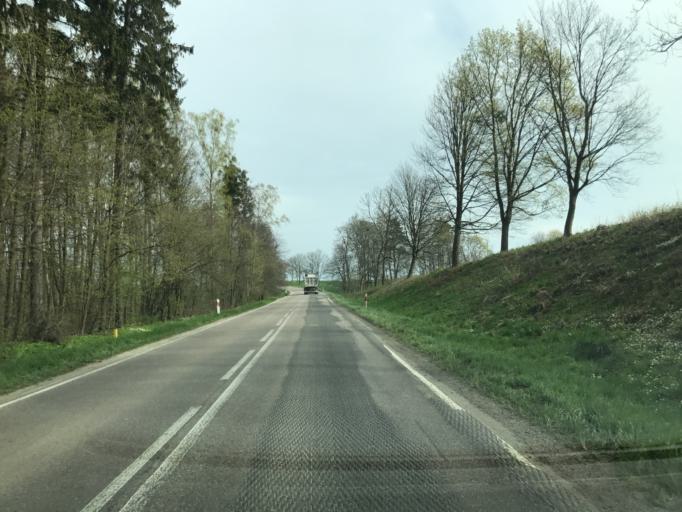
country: PL
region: Warmian-Masurian Voivodeship
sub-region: Powiat ostrodzki
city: Gierzwald
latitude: 53.5605
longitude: 20.0943
